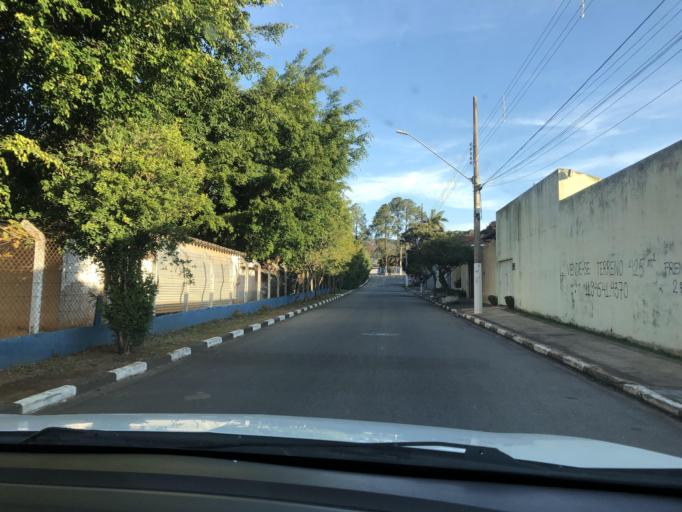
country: BR
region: Sao Paulo
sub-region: Atibaia
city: Atibaia
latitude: -23.1140
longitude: -46.5361
